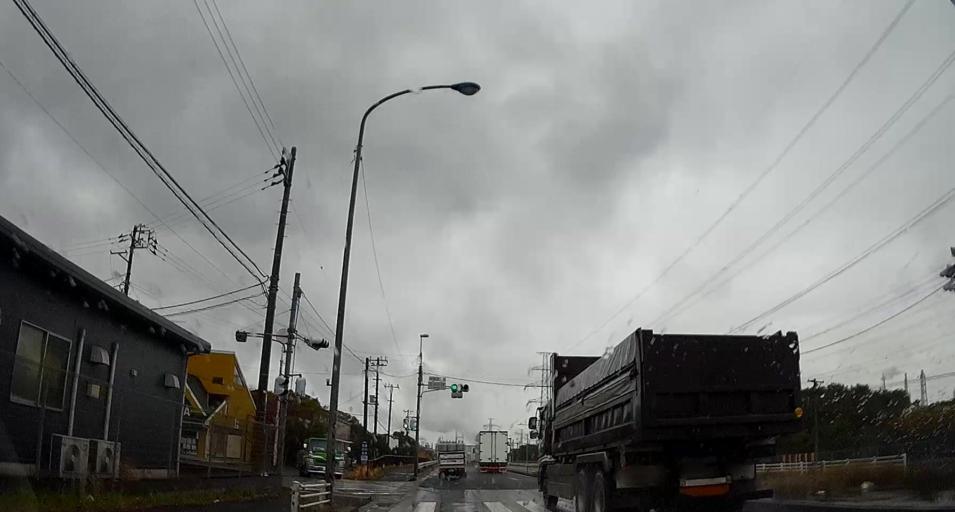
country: JP
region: Chiba
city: Ichihara
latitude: 35.5322
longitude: 140.0855
